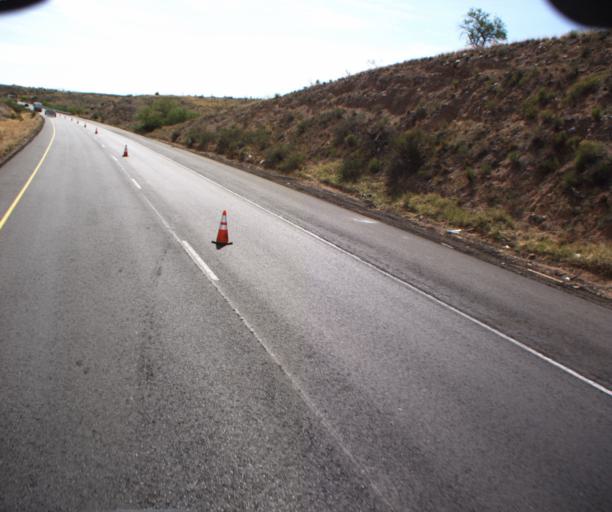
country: US
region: Arizona
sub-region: Pima County
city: Vail
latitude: 31.9965
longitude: -110.6562
